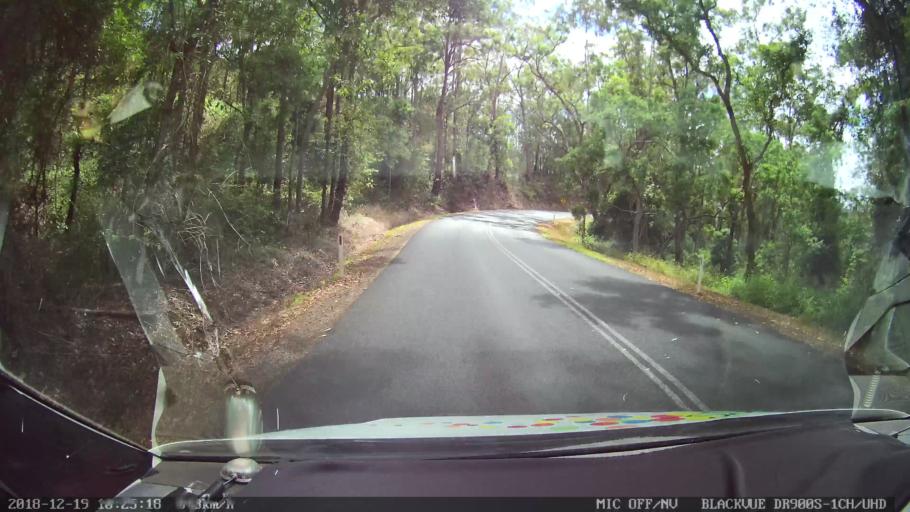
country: AU
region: New South Wales
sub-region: Lismore Municipality
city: Larnook
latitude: -28.5937
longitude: 153.0837
